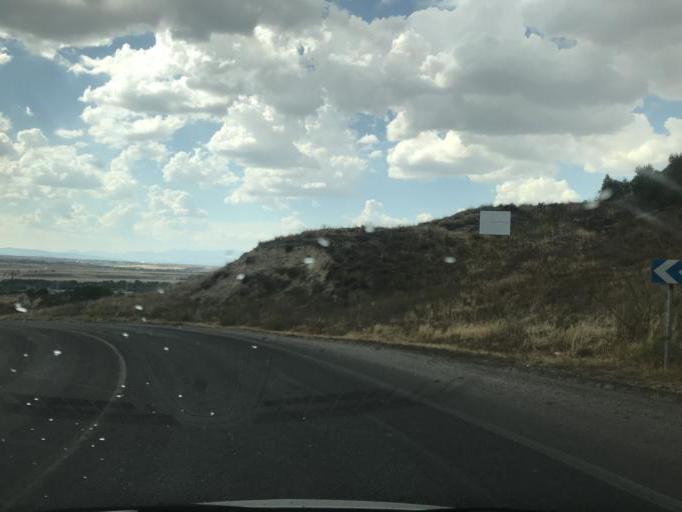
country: ES
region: Madrid
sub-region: Provincia de Madrid
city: Paracuellos de Jarama
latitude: 40.5056
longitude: -3.5349
